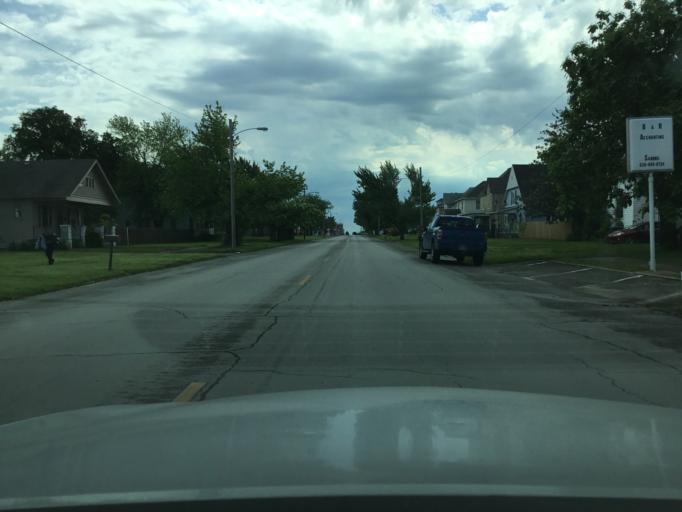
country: US
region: Kansas
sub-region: Montgomery County
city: Coffeyville
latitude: 37.0361
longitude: -95.6268
